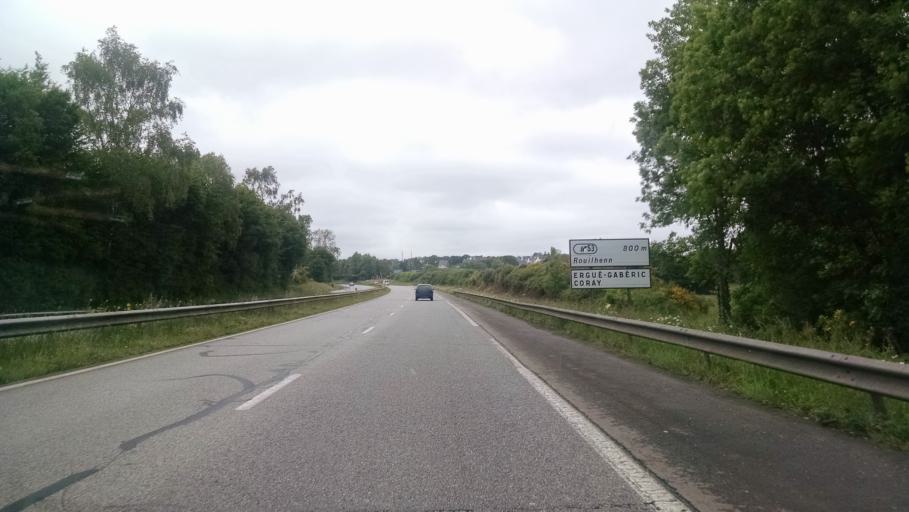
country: FR
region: Brittany
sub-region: Departement du Finistere
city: Quimper
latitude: 48.0071
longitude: -4.0639
